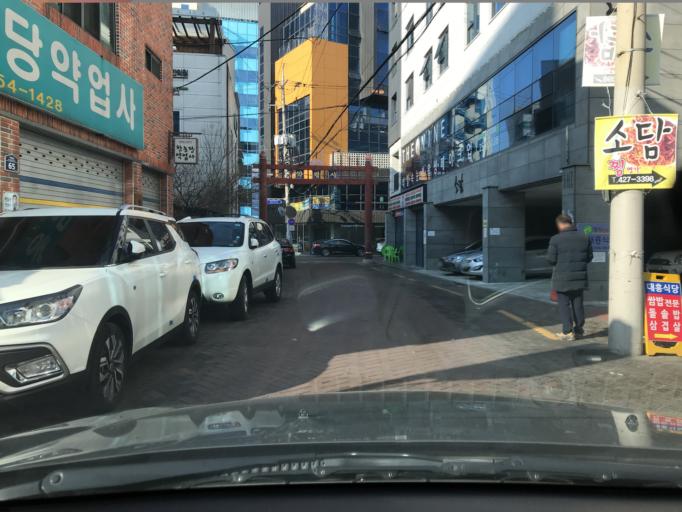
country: KR
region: Daegu
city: Daegu
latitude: 35.8691
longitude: 128.5895
